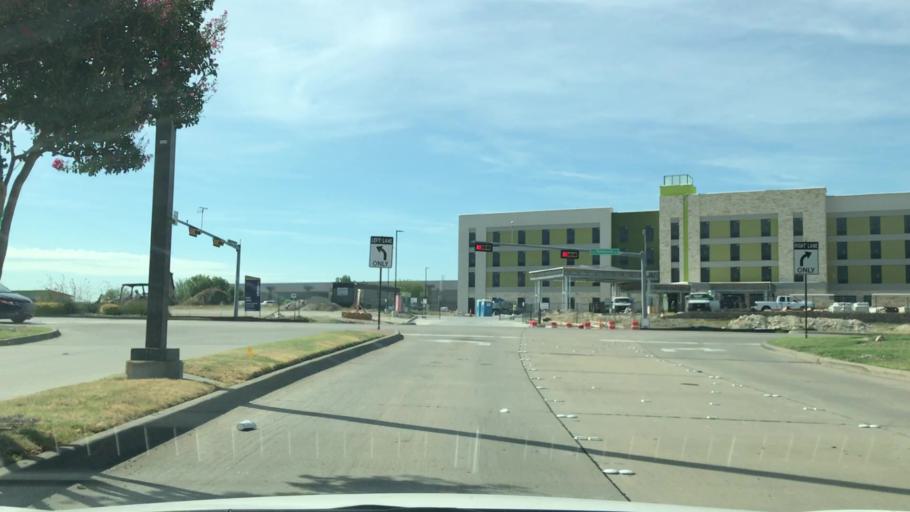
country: US
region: Texas
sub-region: Denton County
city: The Colony
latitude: 33.0712
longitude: -96.8348
